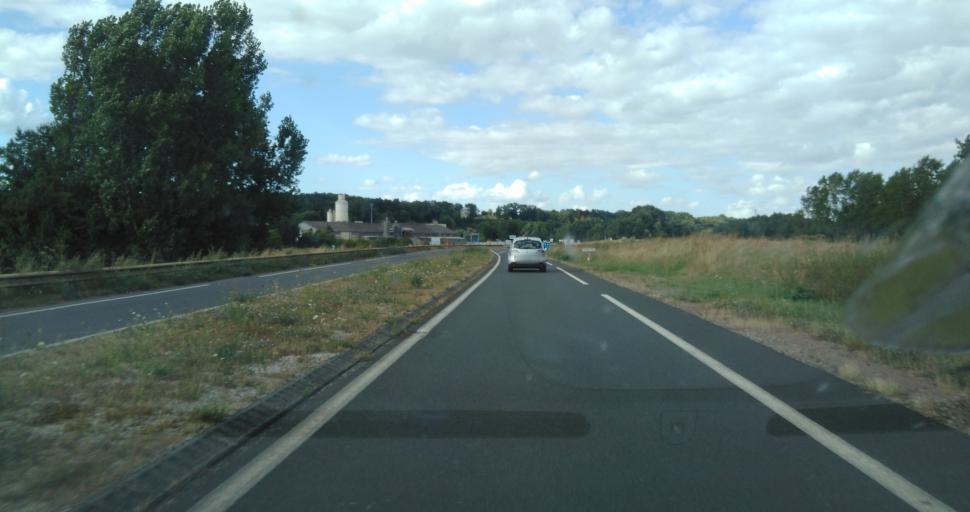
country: FR
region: Centre
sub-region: Departement d'Indre-et-Loire
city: Cinq-Mars-la-Pile
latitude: 47.3408
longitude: 0.4650
